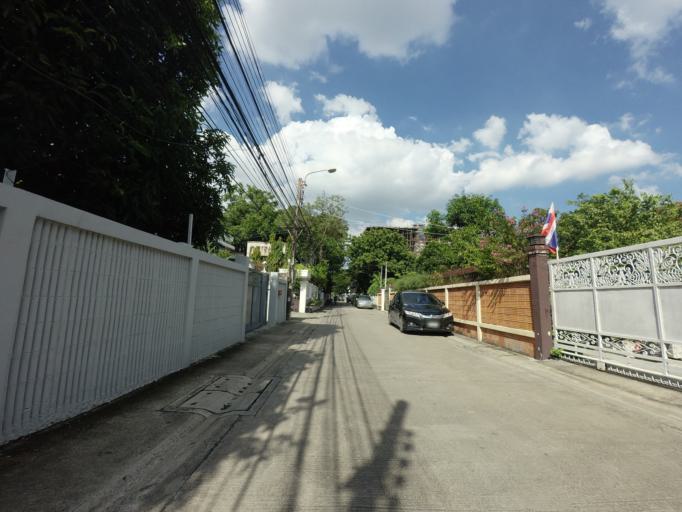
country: TH
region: Bangkok
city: Wang Thonglang
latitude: 13.7875
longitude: 100.5983
